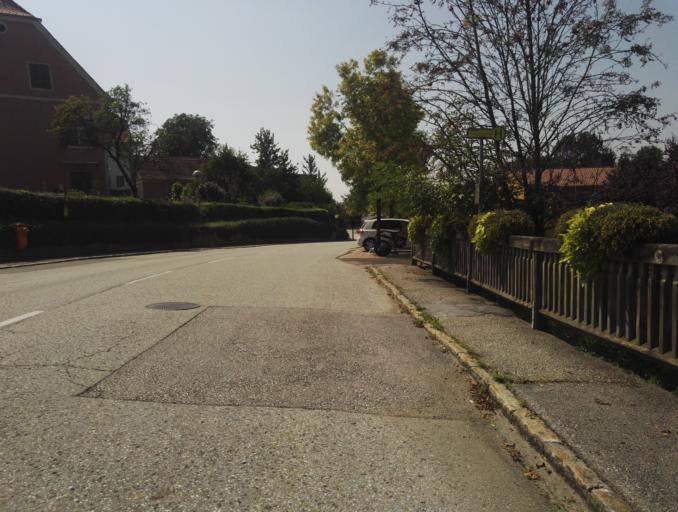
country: AT
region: Styria
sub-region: Politischer Bezirk Graz-Umgebung
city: Sankt Oswald bei Plankenwarth
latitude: 47.0885
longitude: 15.2809
